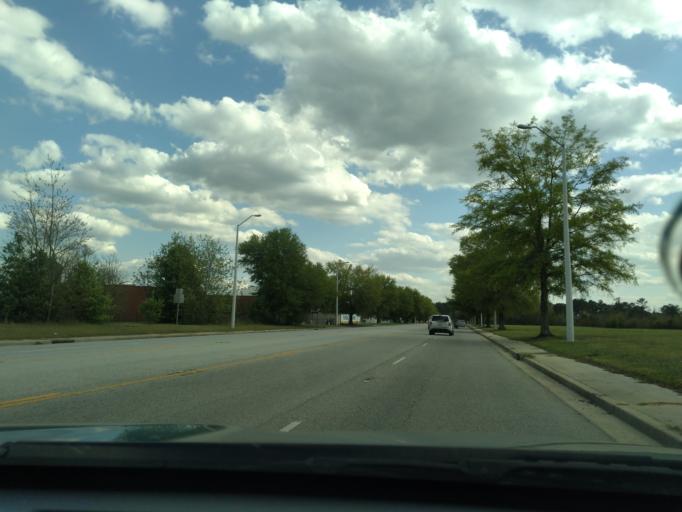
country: US
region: South Carolina
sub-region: Florence County
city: Florence
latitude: 34.1626
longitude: -79.7601
